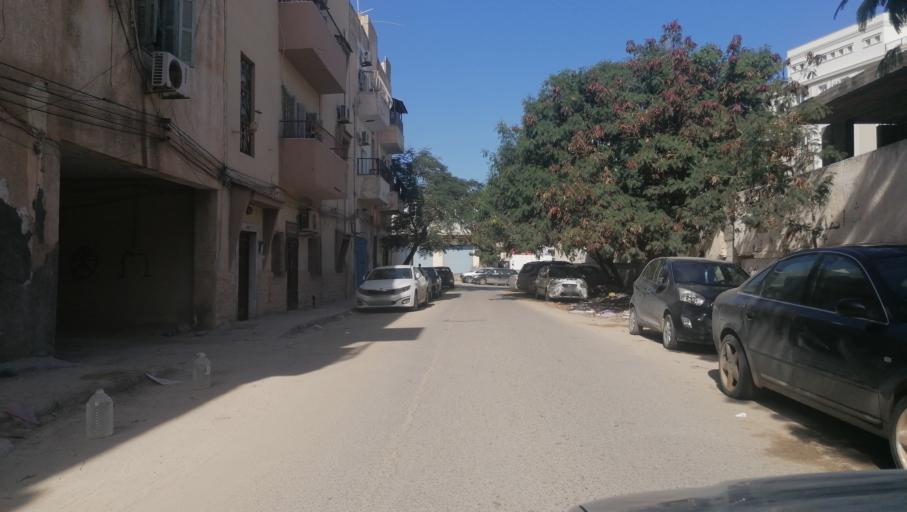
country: LY
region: Tripoli
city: Tripoli
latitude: 32.8912
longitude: 13.1966
